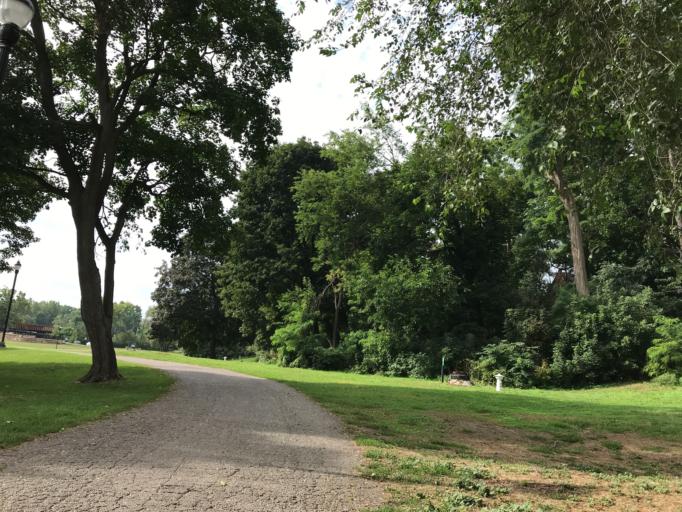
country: US
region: Michigan
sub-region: Washtenaw County
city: Ypsilanti
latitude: 42.2437
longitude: -83.6120
